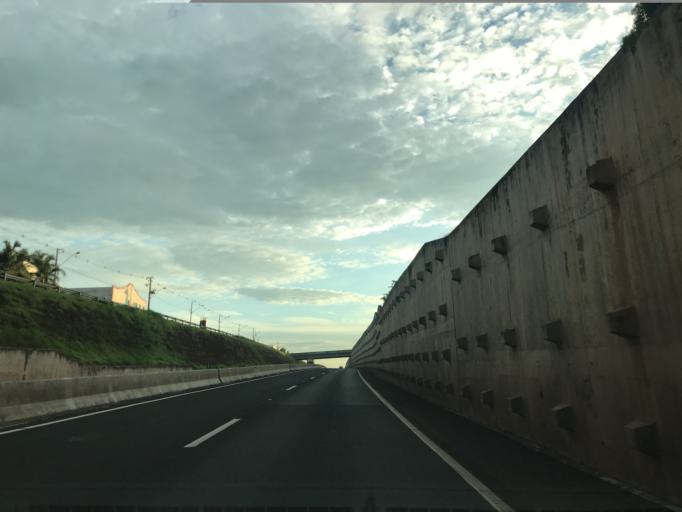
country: BR
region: Parana
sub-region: Maringa
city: Maringa
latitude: -23.3780
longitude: -51.9442
